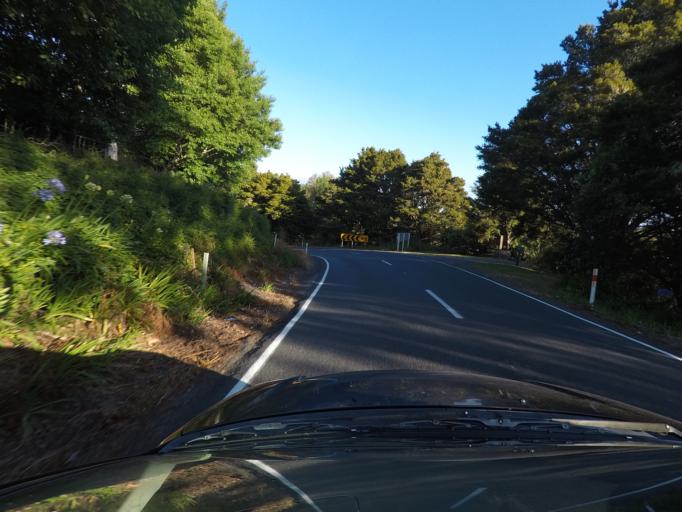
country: NZ
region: Northland
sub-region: Whangarei
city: Whangarei
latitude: -35.6542
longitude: 174.3086
